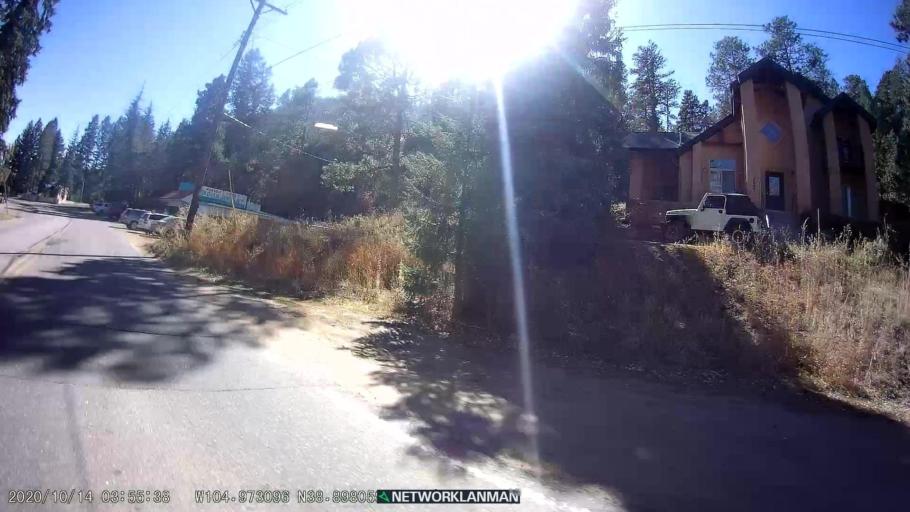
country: US
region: Colorado
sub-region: El Paso County
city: Cascade-Chipita Park
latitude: 38.8969
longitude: -104.9732
